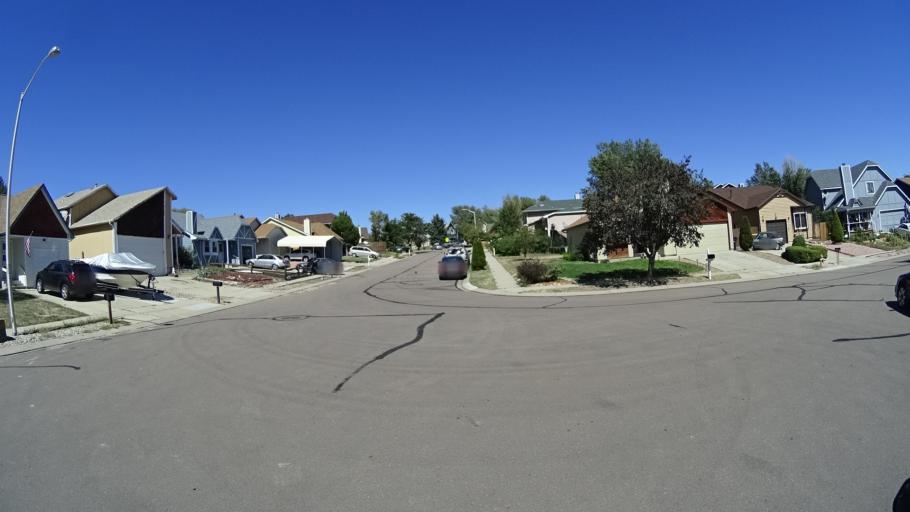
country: US
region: Colorado
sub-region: El Paso County
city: Stratmoor
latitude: 38.7826
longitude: -104.7452
